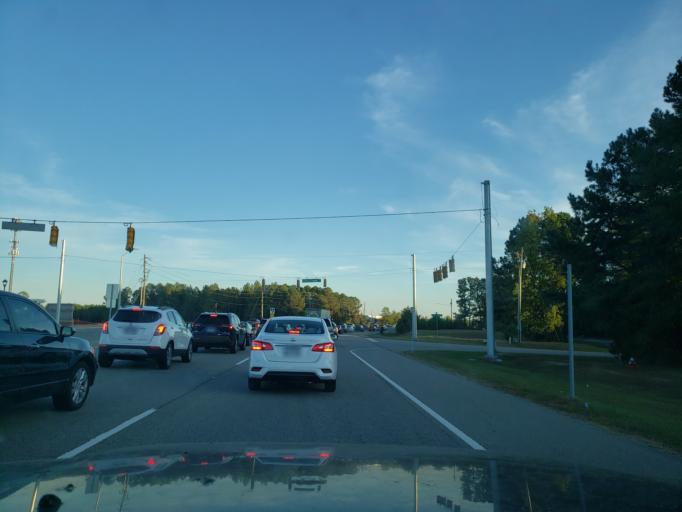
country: US
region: North Carolina
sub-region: Wake County
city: Morrisville
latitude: 35.8256
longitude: -78.8497
